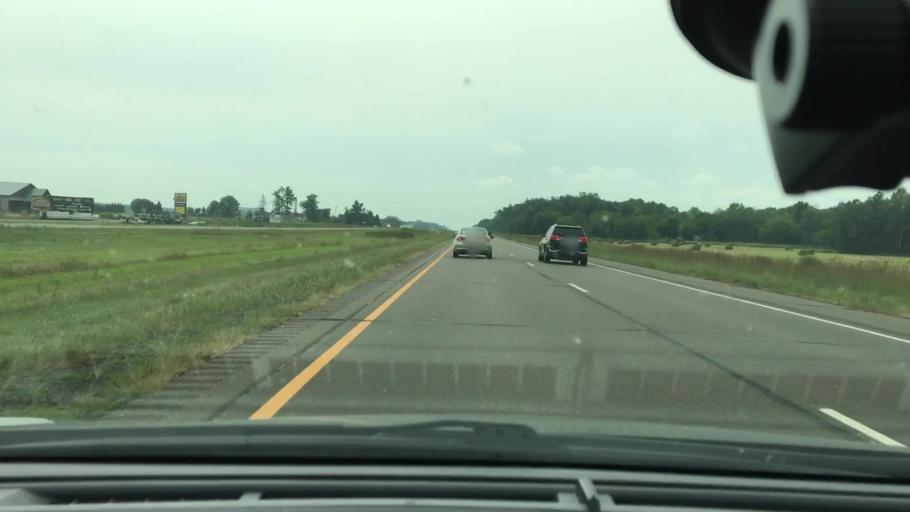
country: US
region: Minnesota
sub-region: Mille Lacs County
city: Vineland
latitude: 46.0411
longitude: -93.6630
